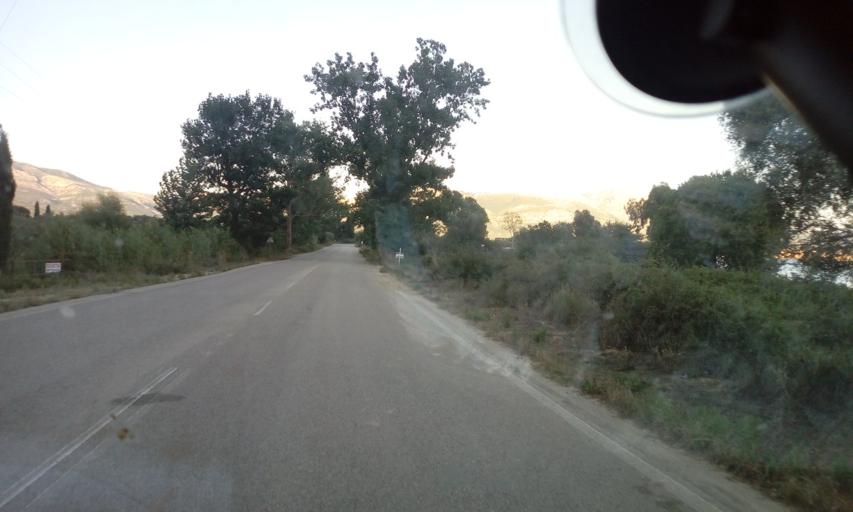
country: GR
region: West Greece
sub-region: Nomos Aitolias kai Akarnanias
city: Kandila
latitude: 38.6784
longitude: 20.9309
